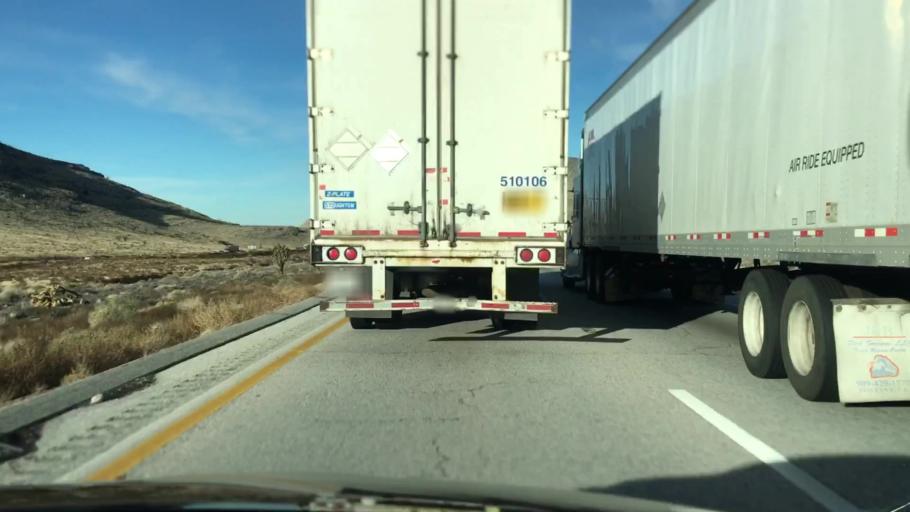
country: US
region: Nevada
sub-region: Clark County
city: Sandy Valley
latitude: 35.4734
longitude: -115.5605
